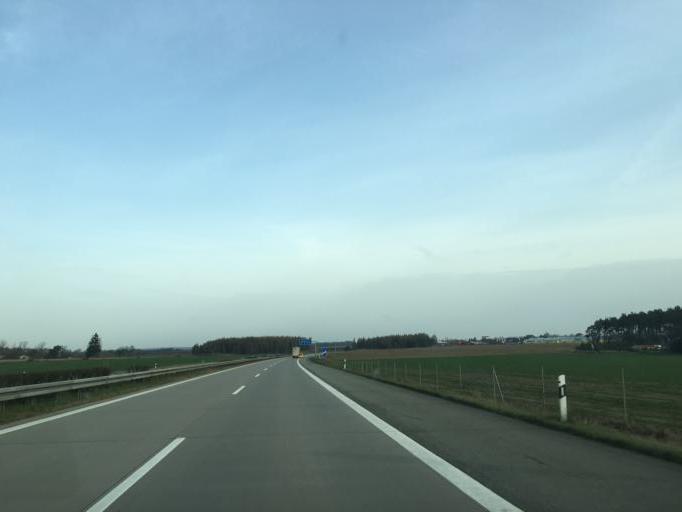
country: DE
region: Brandenburg
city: Wittstock
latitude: 53.1495
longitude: 12.4505
